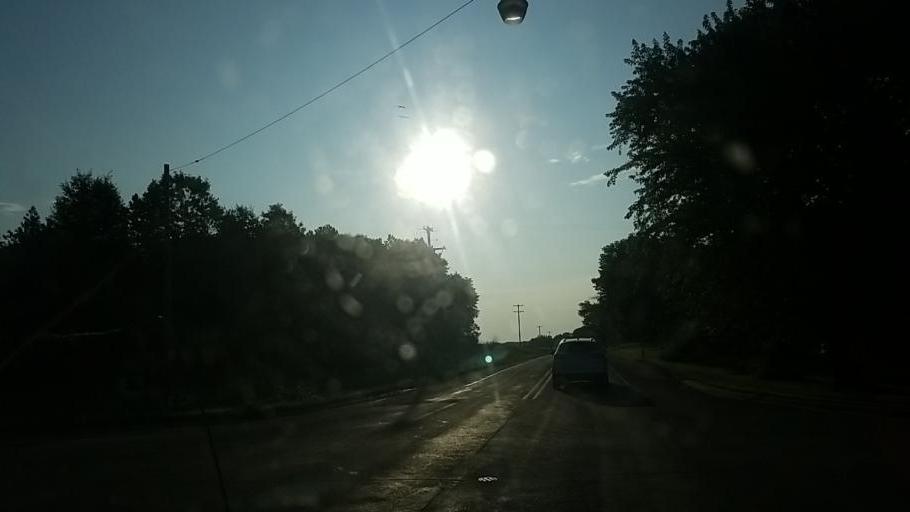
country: US
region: Michigan
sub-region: Montcalm County
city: Greenville
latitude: 43.2497
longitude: -85.2327
